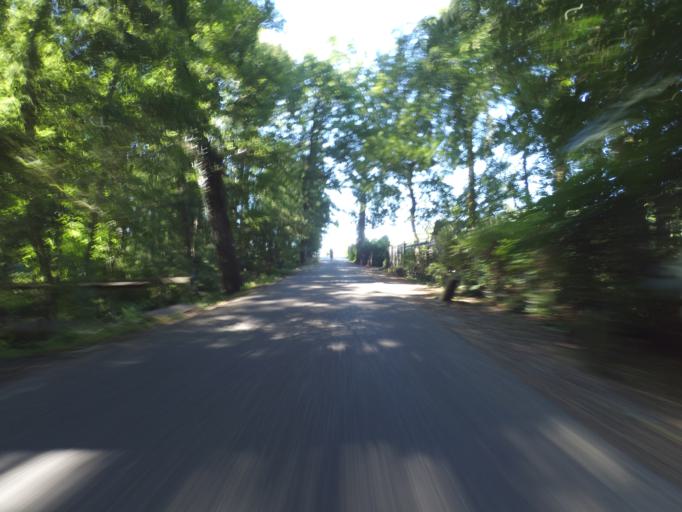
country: NL
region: Utrecht
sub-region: Stichtse Vecht
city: Vreeland
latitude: 52.2054
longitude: 5.0220
